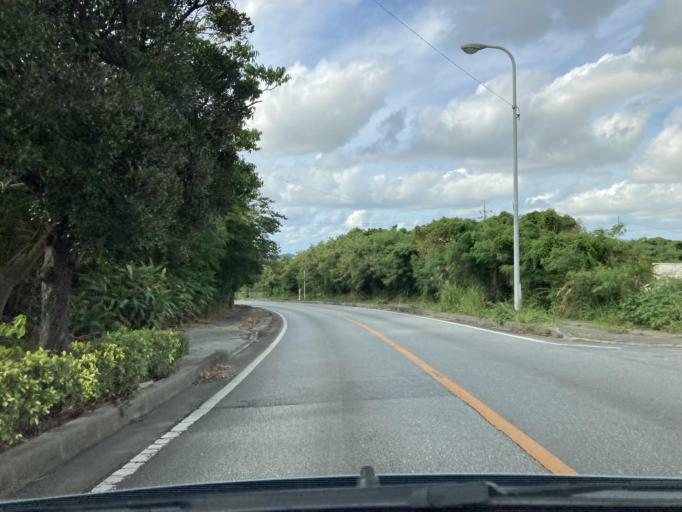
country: JP
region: Okinawa
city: Itoman
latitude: 26.1300
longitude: 127.7101
